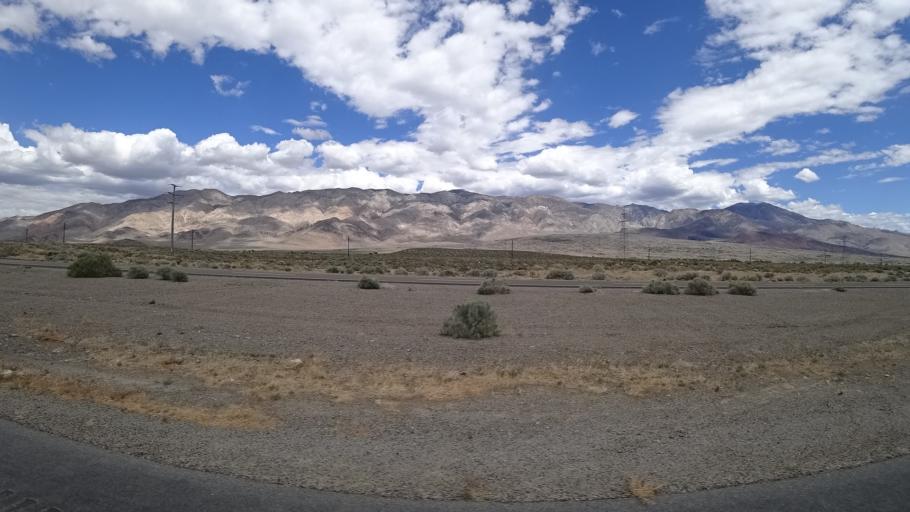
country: US
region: California
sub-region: Inyo County
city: Big Pine
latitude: 37.0446
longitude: -118.2318
